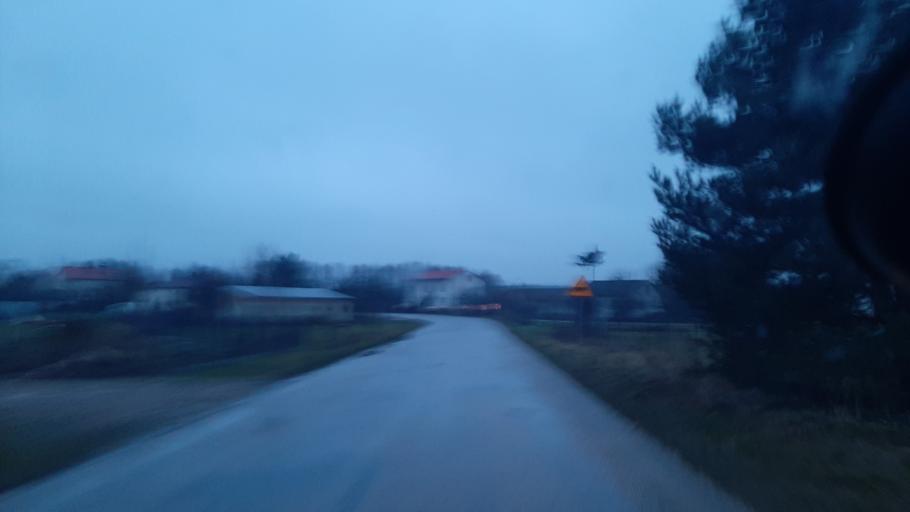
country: PL
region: Lublin Voivodeship
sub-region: Powiat lubelski
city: Garbow
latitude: 51.3955
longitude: 22.4094
